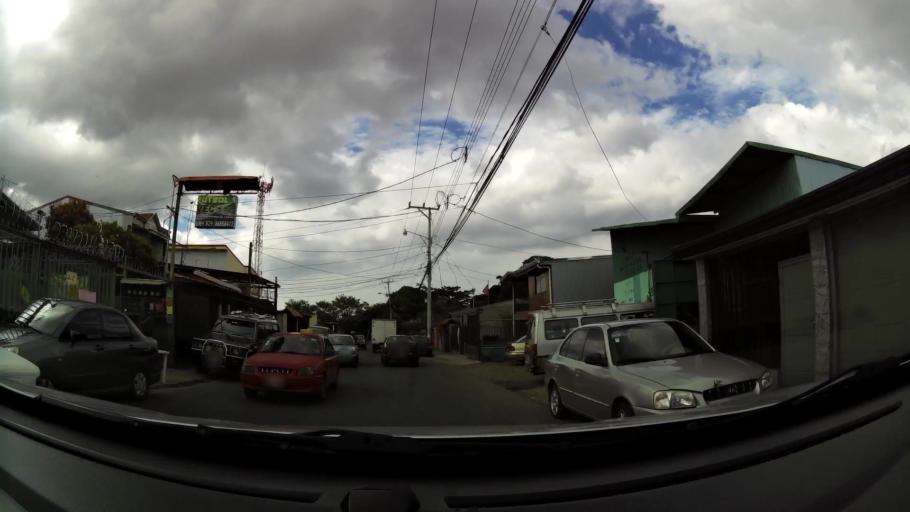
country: CR
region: San Jose
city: Alajuelita
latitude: 9.8948
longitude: -84.0885
